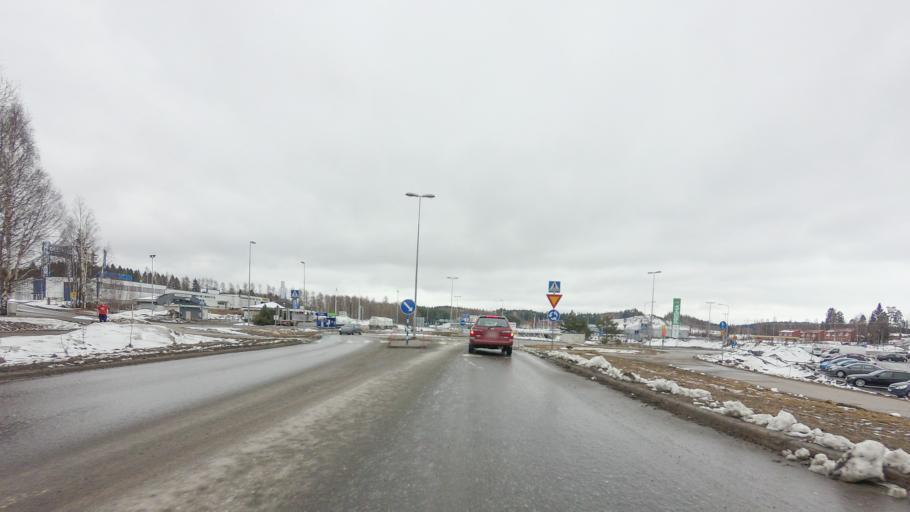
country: FI
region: Southern Savonia
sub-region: Savonlinna
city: Savonlinna
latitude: 61.8768
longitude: 28.9501
